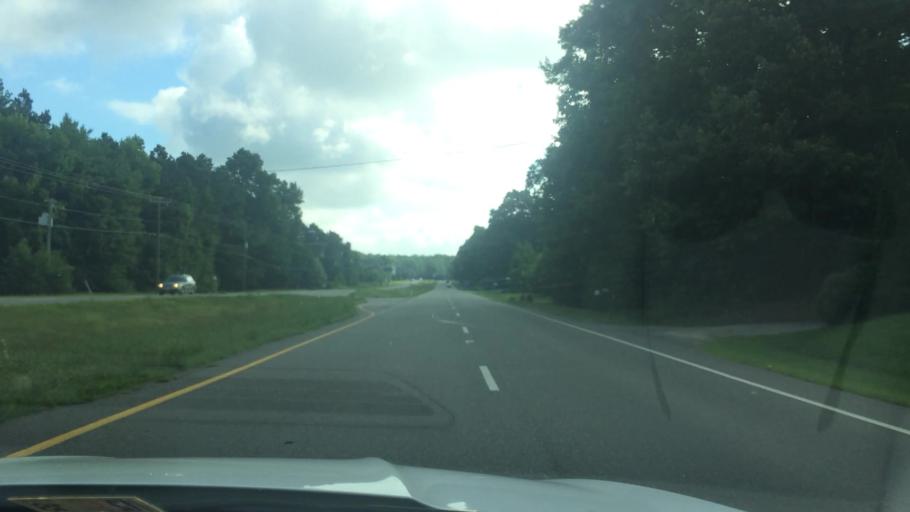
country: US
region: Virginia
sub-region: Gloucester County
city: Gloucester Courthouse
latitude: 37.4613
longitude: -76.4664
